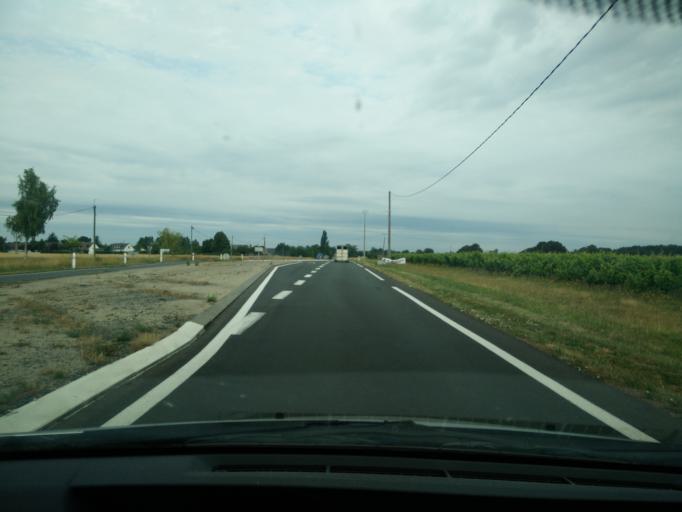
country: FR
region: Pays de la Loire
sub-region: Departement de Maine-et-Loire
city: Brissac-Quince
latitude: 47.3256
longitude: -0.4162
